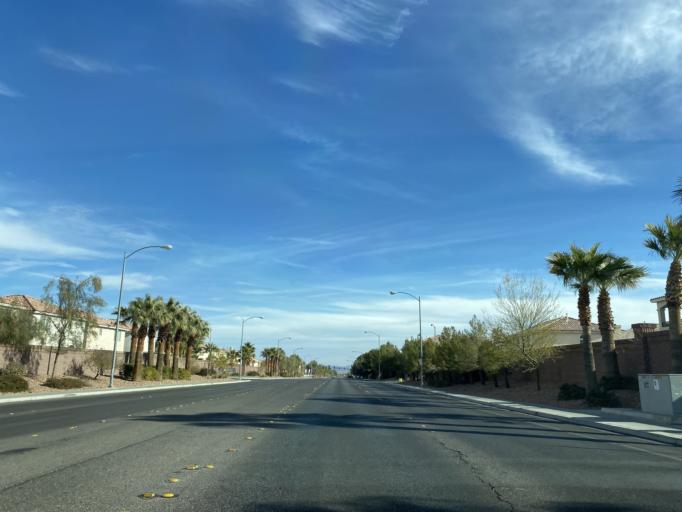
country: US
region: Nevada
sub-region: Clark County
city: Enterprise
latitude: 36.0491
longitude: -115.2292
